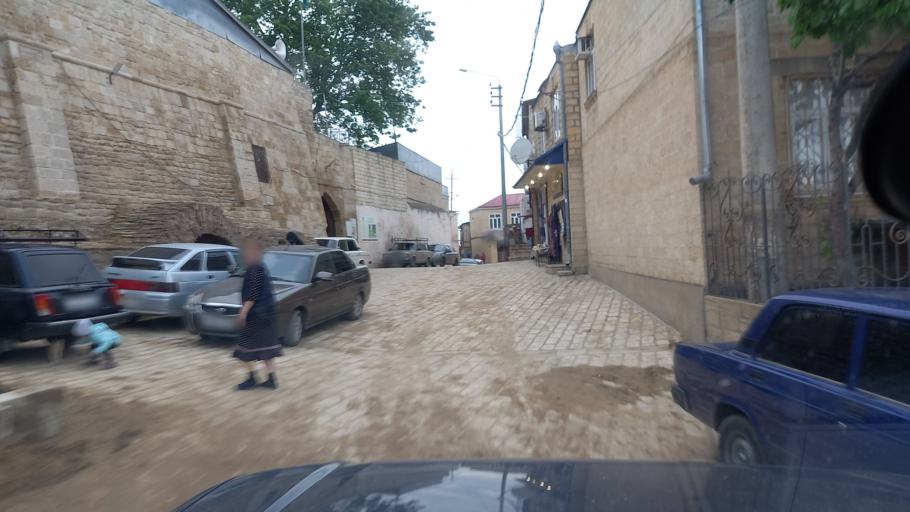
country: RU
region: Dagestan
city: Derbent
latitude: 42.0551
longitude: 48.2804
